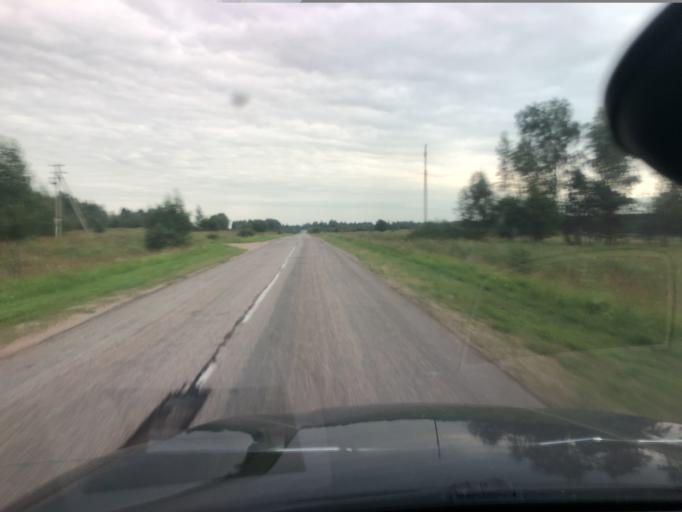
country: RU
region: Jaroslavl
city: Petrovsk
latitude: 57.0025
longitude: 39.0292
